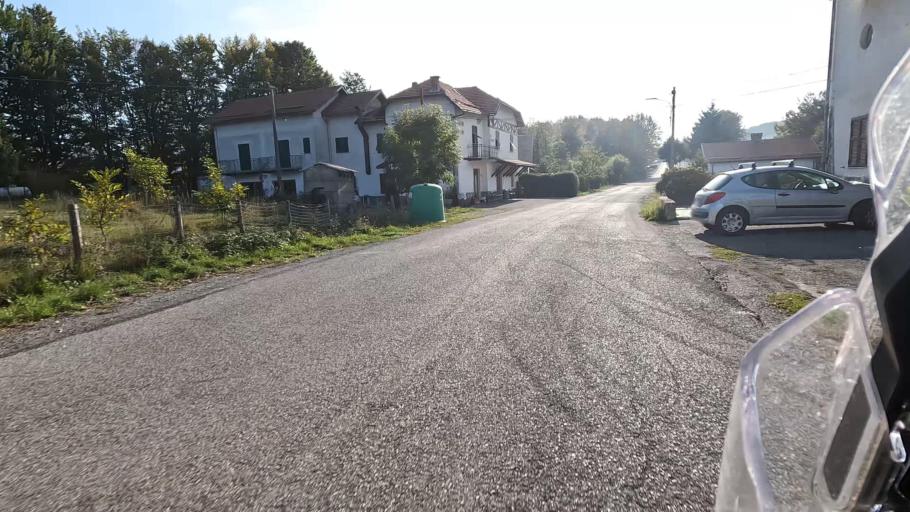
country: IT
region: Liguria
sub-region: Provincia di Savona
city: Urbe
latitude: 44.4690
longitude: 8.5599
